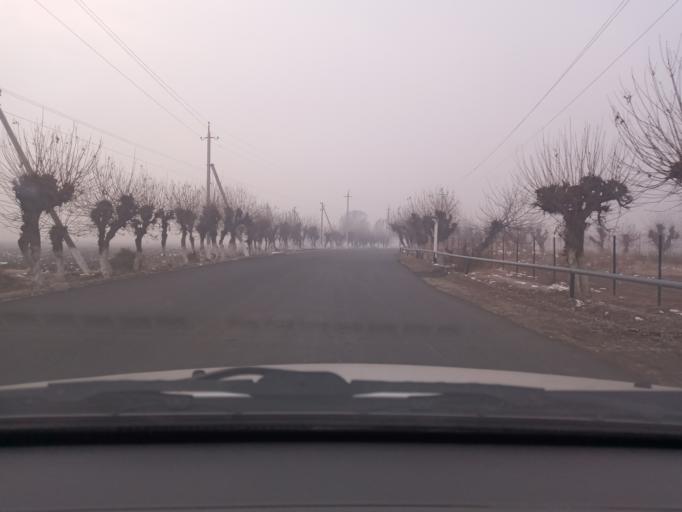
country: UZ
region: Namangan
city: Pop
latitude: 40.8700
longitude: 71.1468
